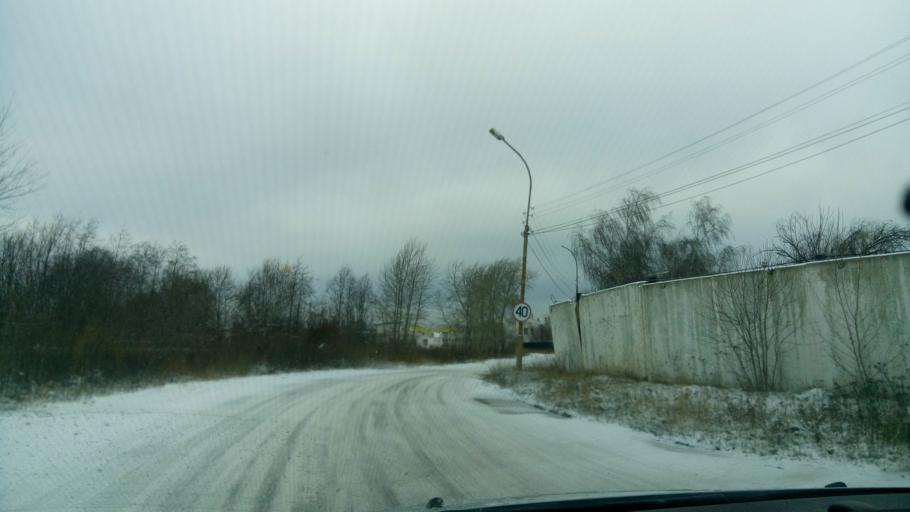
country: RU
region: Sverdlovsk
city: Polevskoy
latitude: 56.4654
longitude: 60.1793
